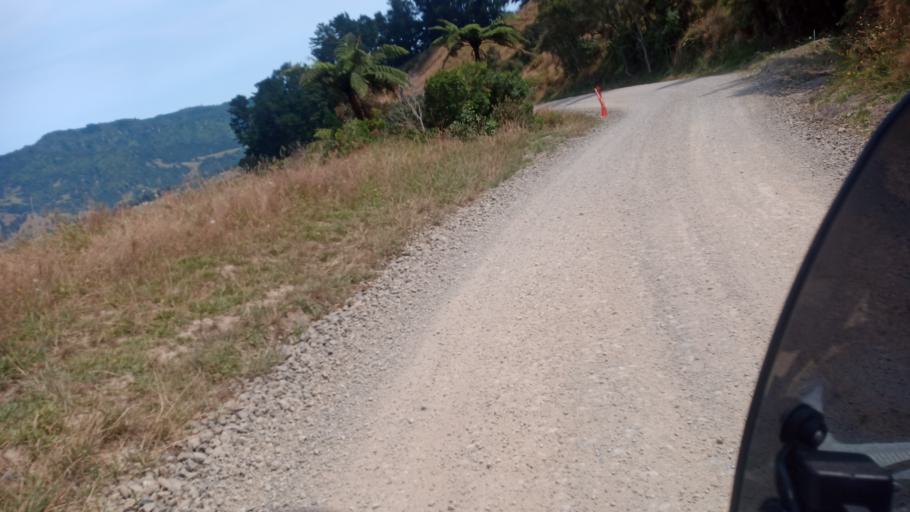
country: NZ
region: Bay of Plenty
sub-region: Opotiki District
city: Opotiki
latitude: -37.6589
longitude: 178.1294
